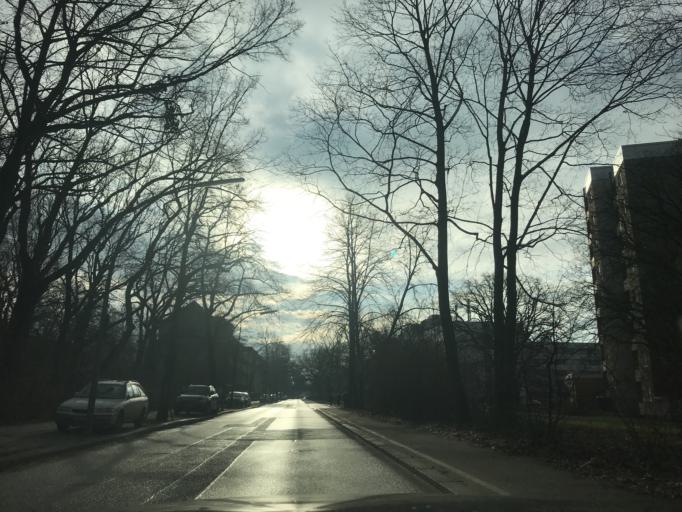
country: DE
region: Berlin
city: Siemensstadt
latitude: 52.5424
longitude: 13.2620
